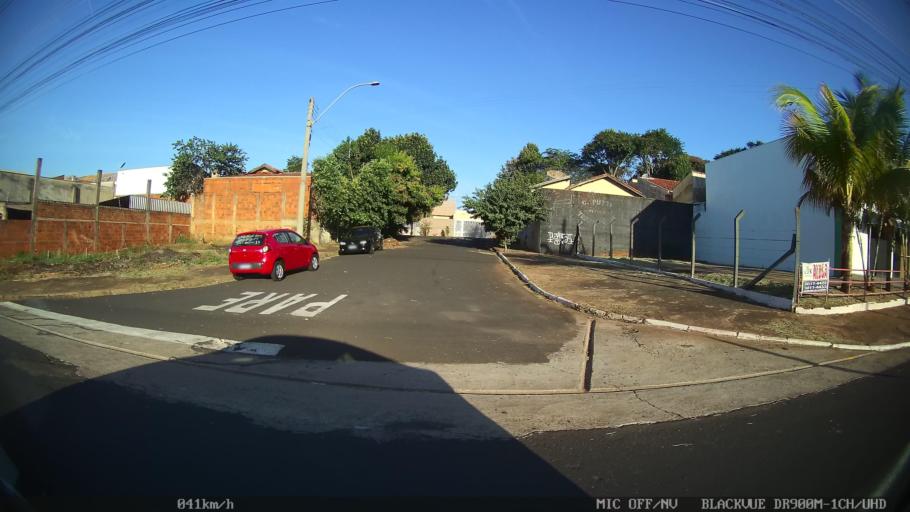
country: BR
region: Sao Paulo
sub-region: Sao Jose Do Rio Preto
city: Sao Jose do Rio Preto
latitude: -20.7929
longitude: -49.3523
